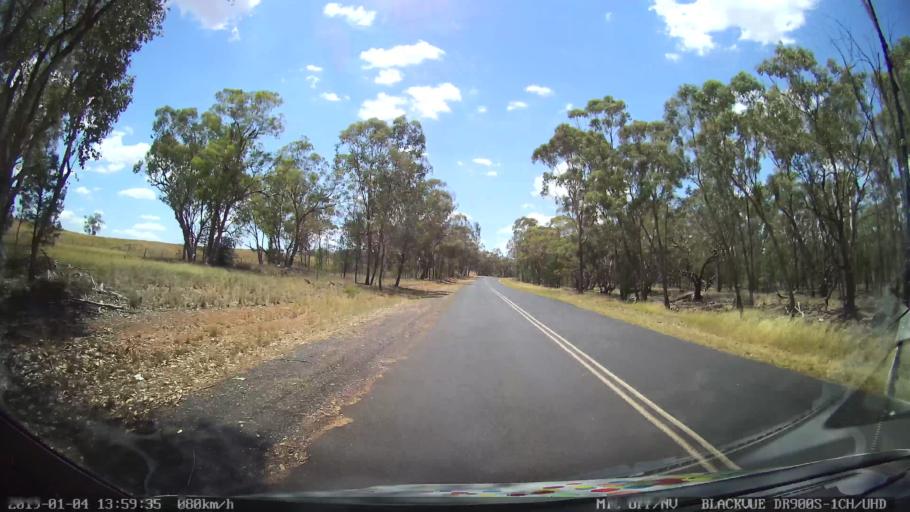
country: AU
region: New South Wales
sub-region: Dubbo Municipality
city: Dubbo
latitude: -32.3153
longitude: 148.5888
